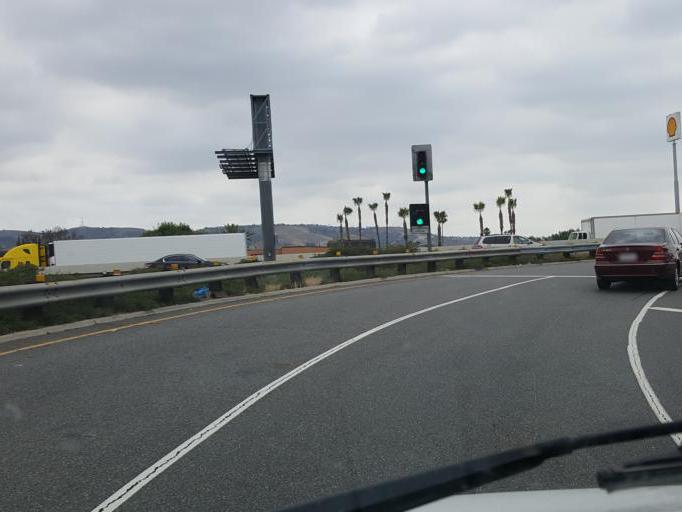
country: US
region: California
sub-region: Los Angeles County
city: South San Jose Hills
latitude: 33.9949
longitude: -117.9040
